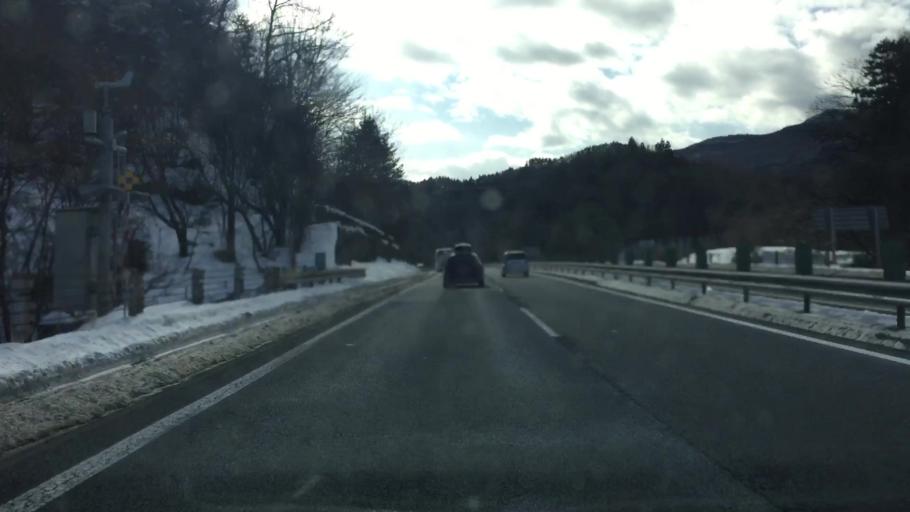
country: JP
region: Gunma
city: Numata
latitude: 36.7389
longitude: 138.9765
